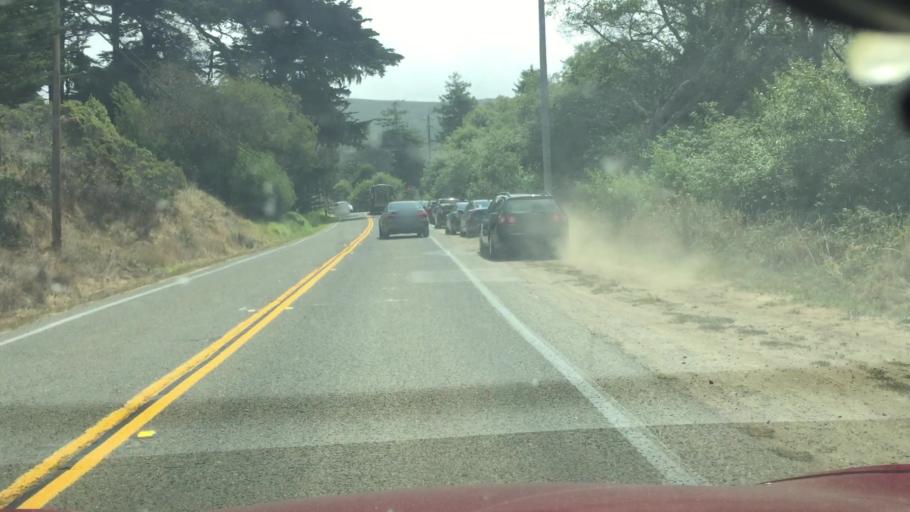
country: US
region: California
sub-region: Marin County
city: Tamalpais Valley
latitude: 37.8677
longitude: -122.5783
